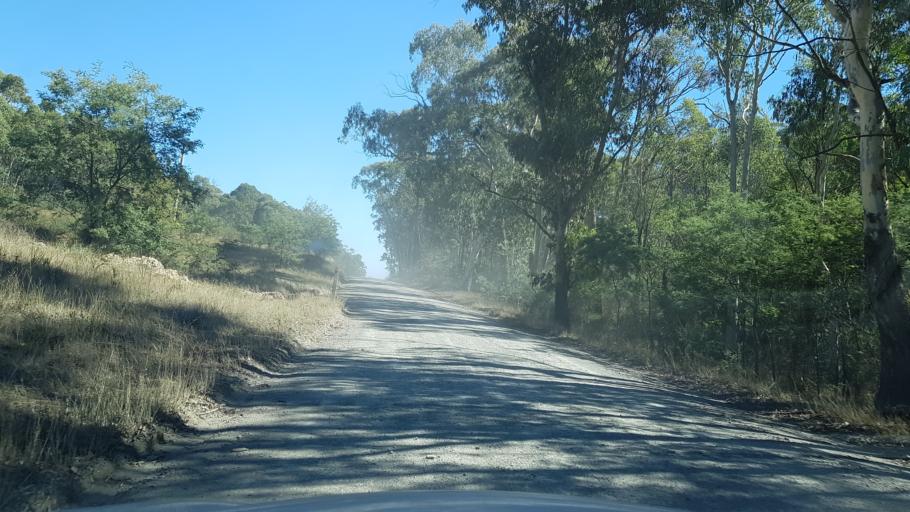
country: AU
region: Victoria
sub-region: Mansfield
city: Mansfield
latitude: -36.8455
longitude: 146.5037
